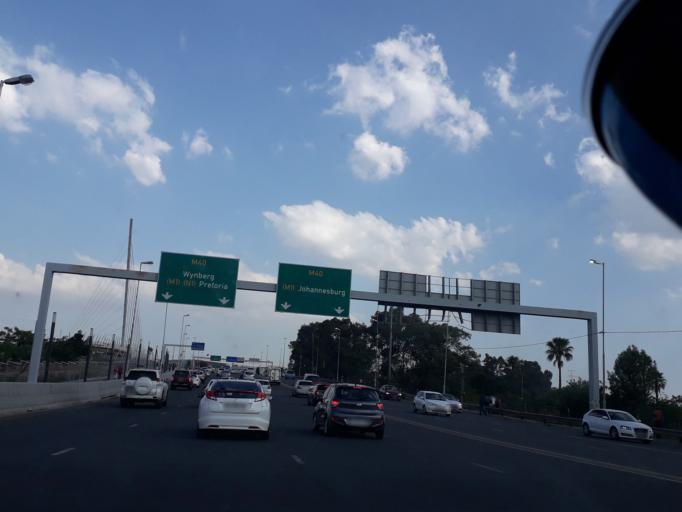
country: ZA
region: Gauteng
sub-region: City of Johannesburg Metropolitan Municipality
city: Modderfontein
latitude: -26.1055
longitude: 28.0738
